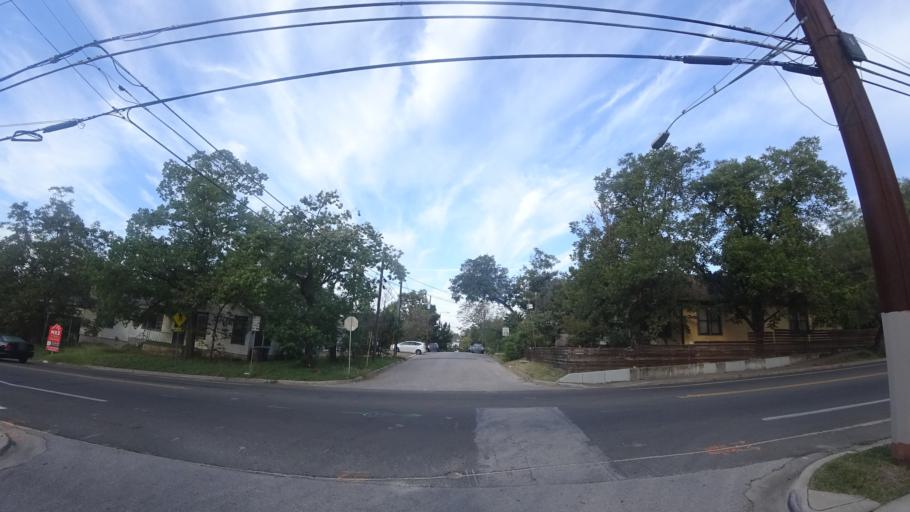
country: US
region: Texas
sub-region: Travis County
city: Austin
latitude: 30.2793
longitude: -97.7169
